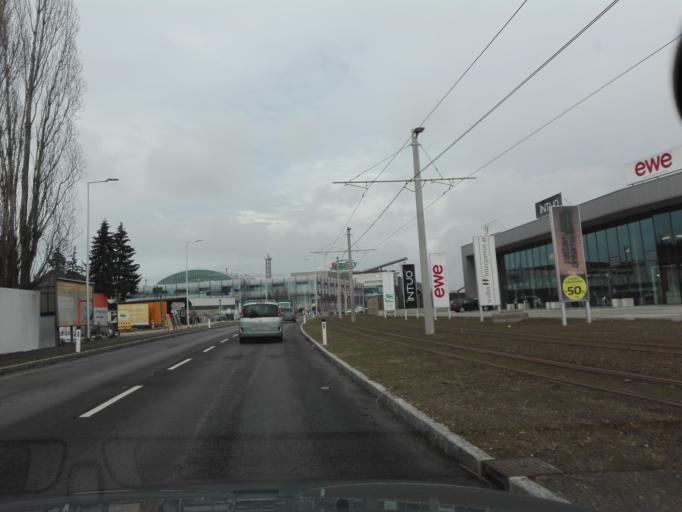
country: AT
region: Upper Austria
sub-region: Politischer Bezirk Linz-Land
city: Traun
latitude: 48.2399
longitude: 14.2346
